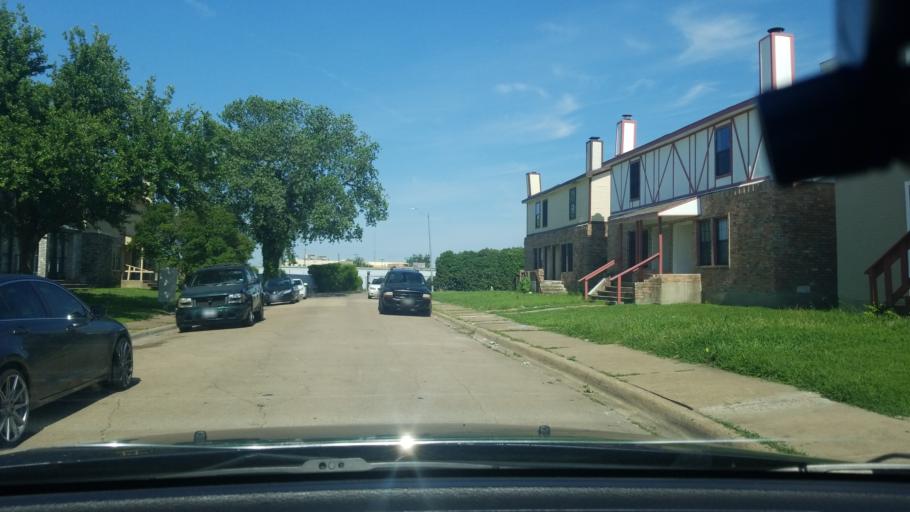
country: US
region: Texas
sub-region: Dallas County
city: Mesquite
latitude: 32.7783
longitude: -96.5951
